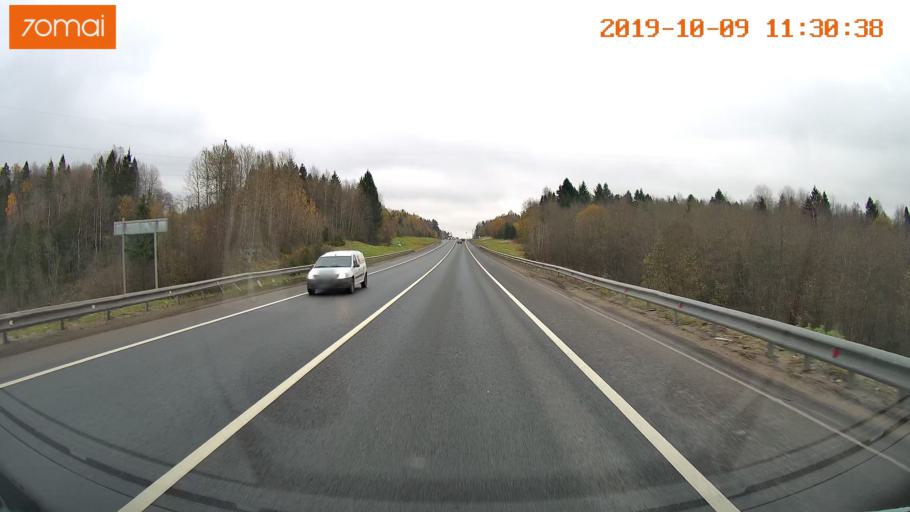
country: RU
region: Vologda
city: Gryazovets
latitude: 59.0521
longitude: 40.0796
